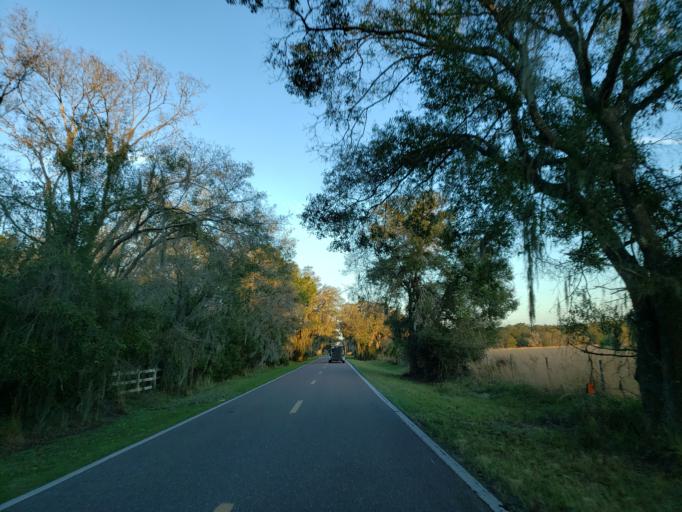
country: US
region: Florida
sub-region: Hillsborough County
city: Fish Hawk
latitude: 27.8287
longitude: -82.1941
